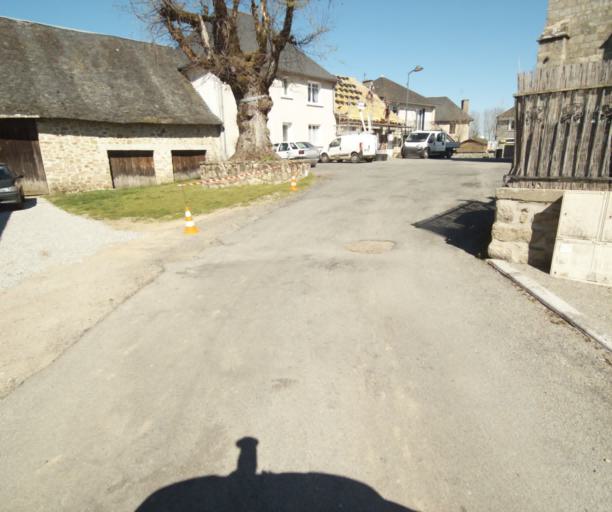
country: FR
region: Limousin
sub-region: Departement de la Correze
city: Saint-Mexant
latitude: 45.3100
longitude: 1.6351
